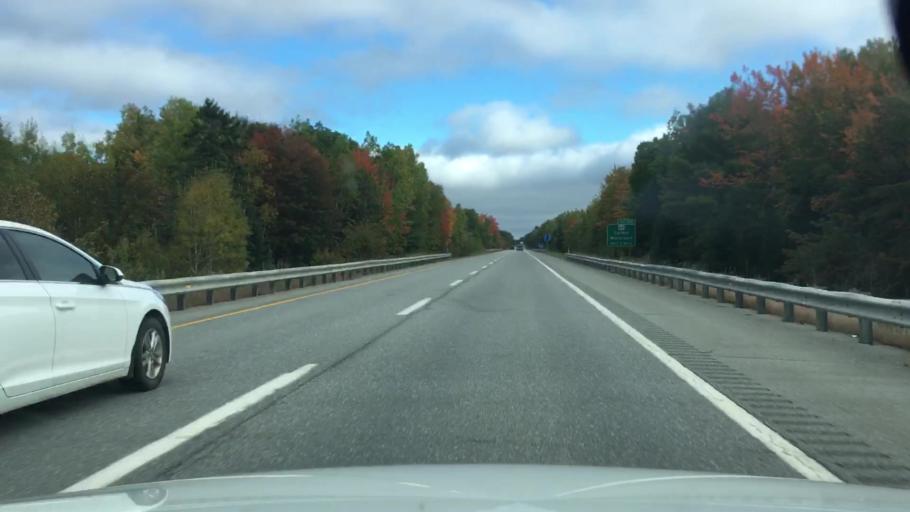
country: US
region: Maine
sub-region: Penobscot County
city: Carmel
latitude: 44.7679
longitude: -68.9974
